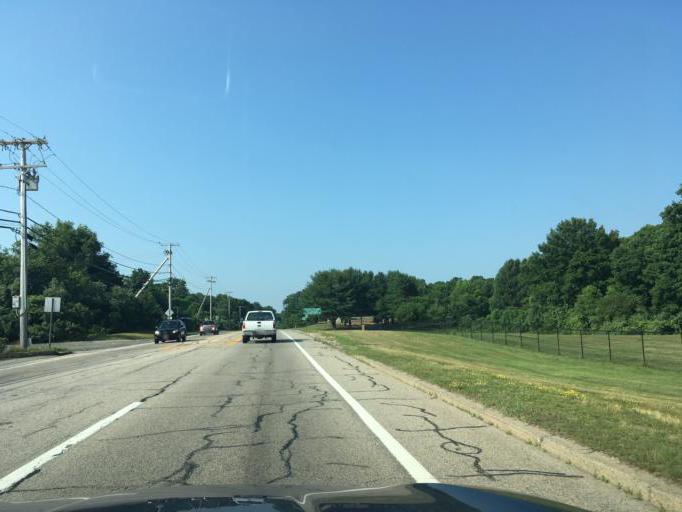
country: US
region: Rhode Island
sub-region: Washington County
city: Exeter
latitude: 41.5467
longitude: -71.5339
